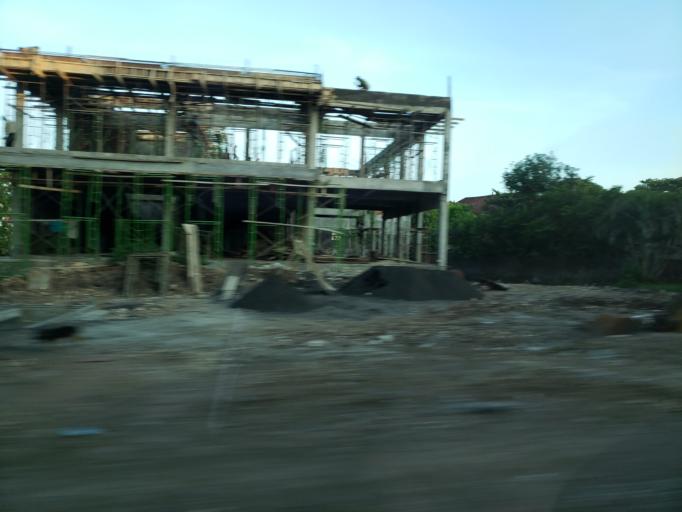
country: ID
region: Bali
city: Jimbaran
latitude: -8.7947
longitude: 115.1761
